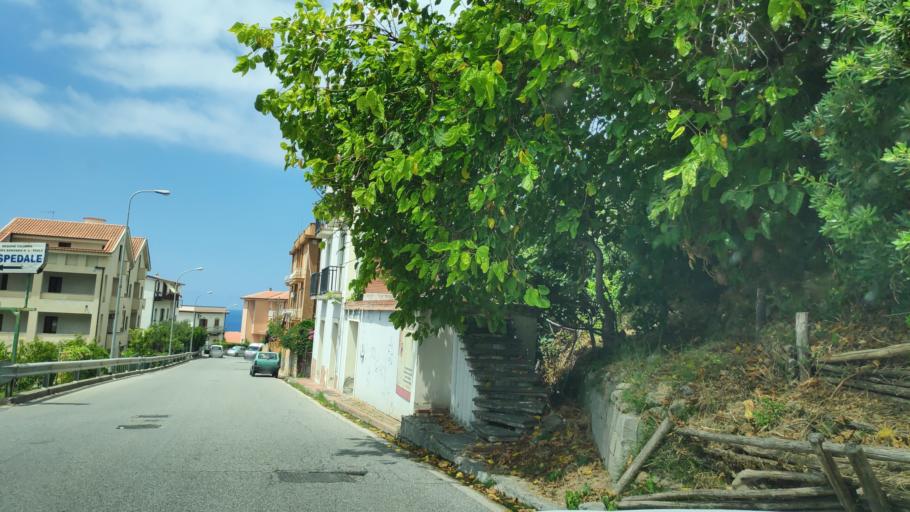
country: IT
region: Calabria
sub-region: Provincia di Cosenza
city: Paola
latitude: 39.3538
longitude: 16.0434
